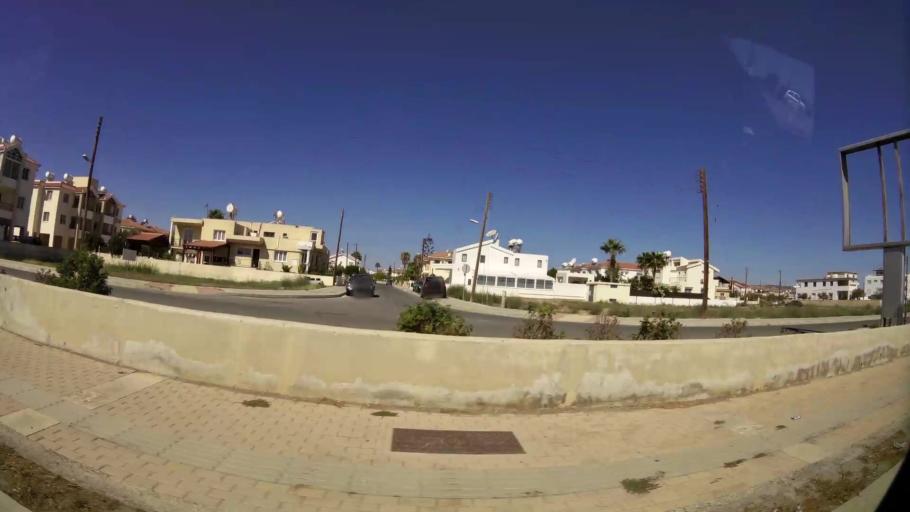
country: CY
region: Larnaka
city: Livadia
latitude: 34.9540
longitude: 33.6512
